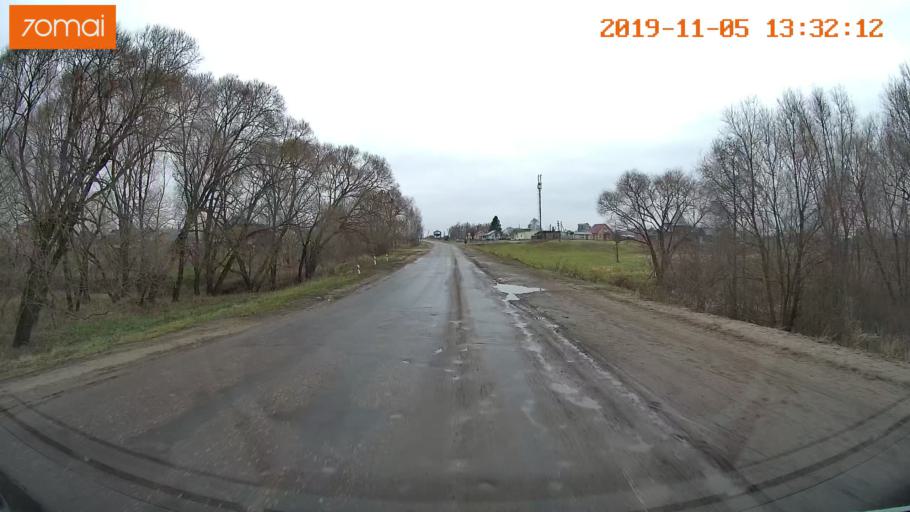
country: RU
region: Ivanovo
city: Shuya
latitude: 56.8814
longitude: 41.3983
